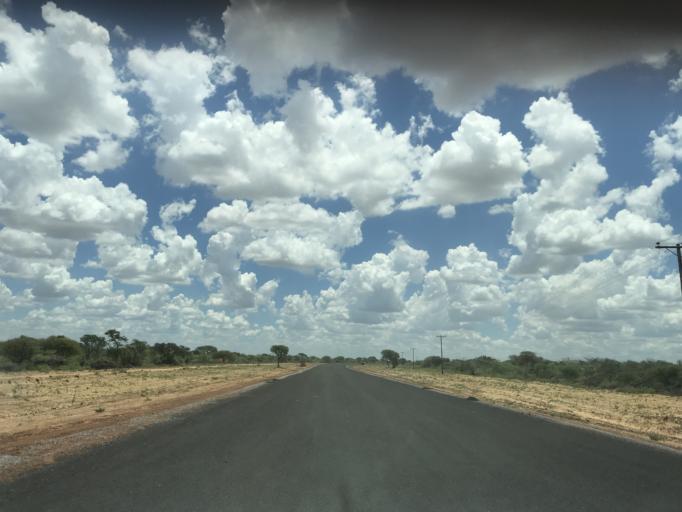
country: BW
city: Mabuli
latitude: -25.8028
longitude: 24.6730
